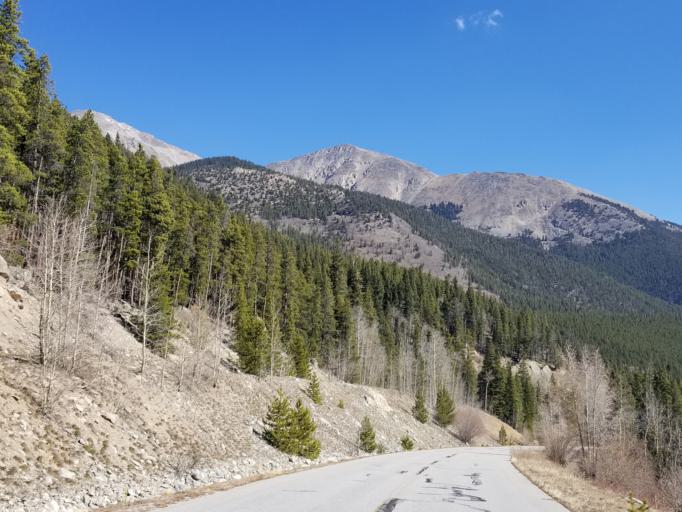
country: US
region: Colorado
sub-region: Chaffee County
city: Buena Vista
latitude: 38.8143
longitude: -106.3435
